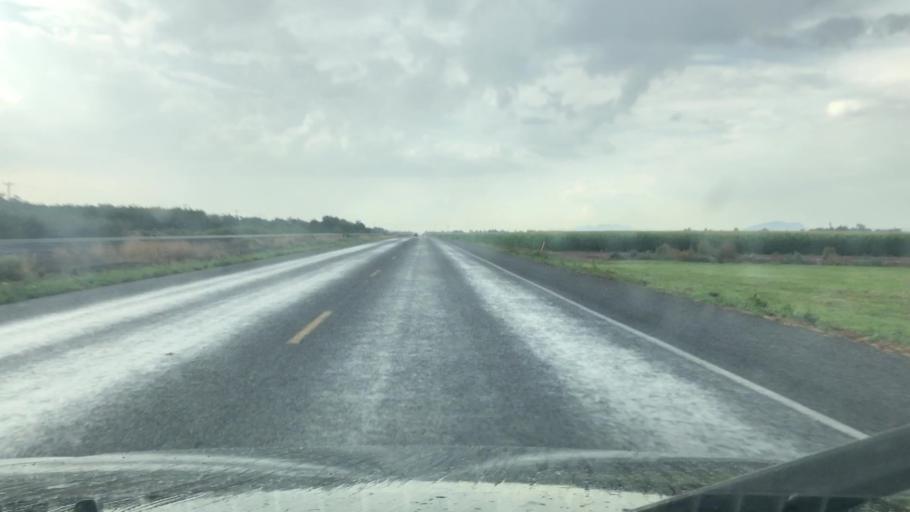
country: US
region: New Mexico
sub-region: Dona Ana County
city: Mesquite
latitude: 32.1386
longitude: -106.6801
